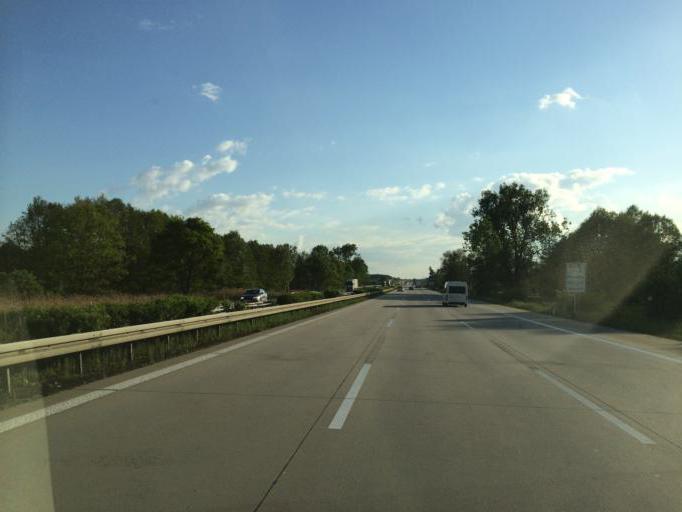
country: DE
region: Brandenburg
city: Ziesar
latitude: 52.2589
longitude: 12.3260
